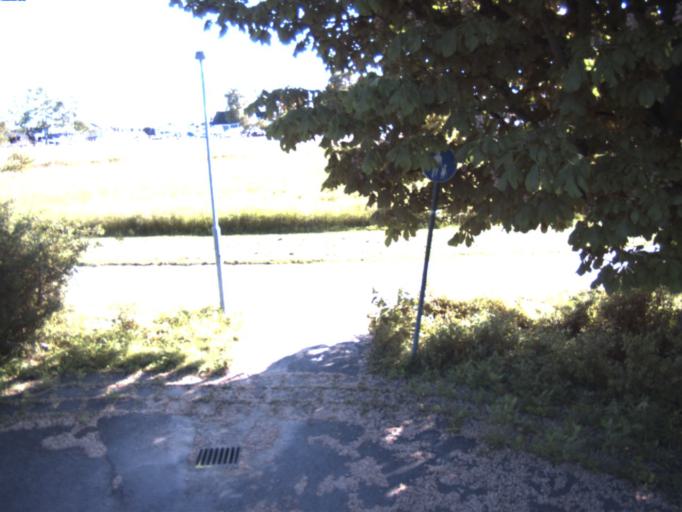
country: SE
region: Skane
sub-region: Helsingborg
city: Rydeback
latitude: 55.9967
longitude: 12.7461
